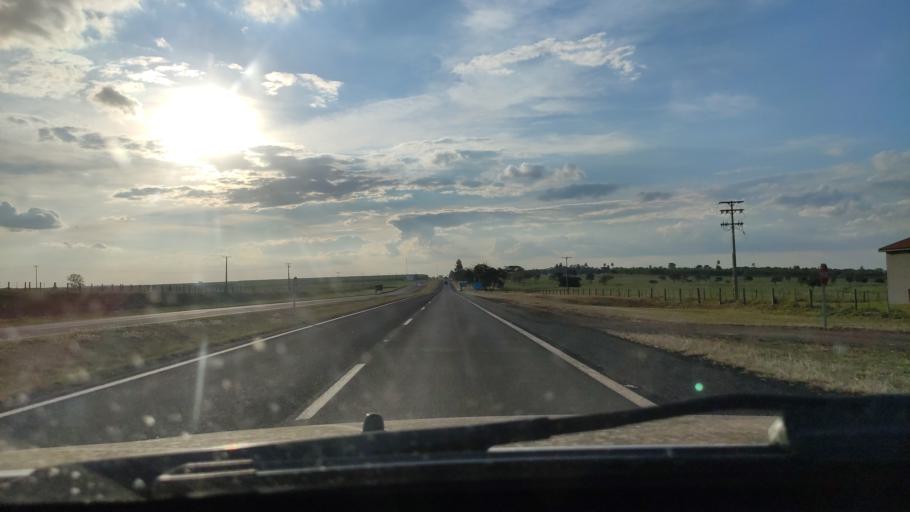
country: BR
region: Sao Paulo
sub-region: Rancharia
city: Rancharia
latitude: -22.4537
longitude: -50.9767
